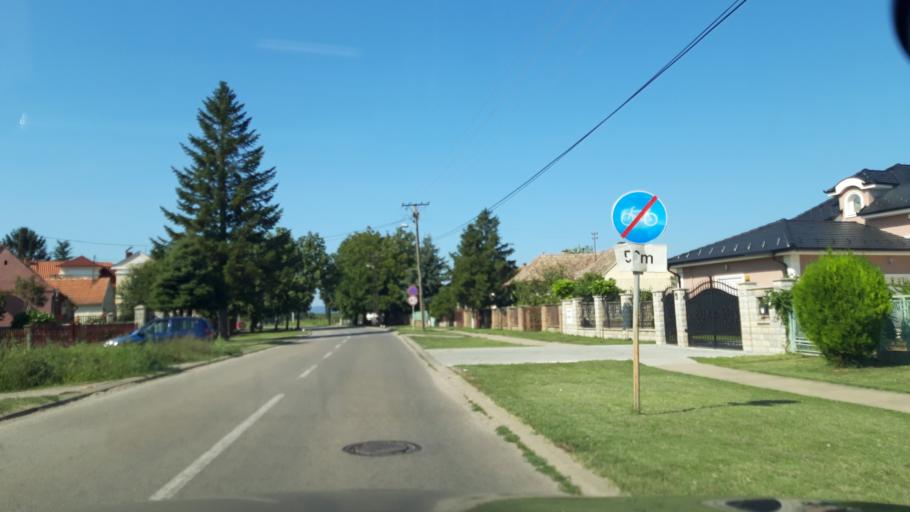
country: RS
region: Autonomna Pokrajina Vojvodina
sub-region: Sremski Okrug
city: Ruma
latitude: 45.0215
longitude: 19.8216
